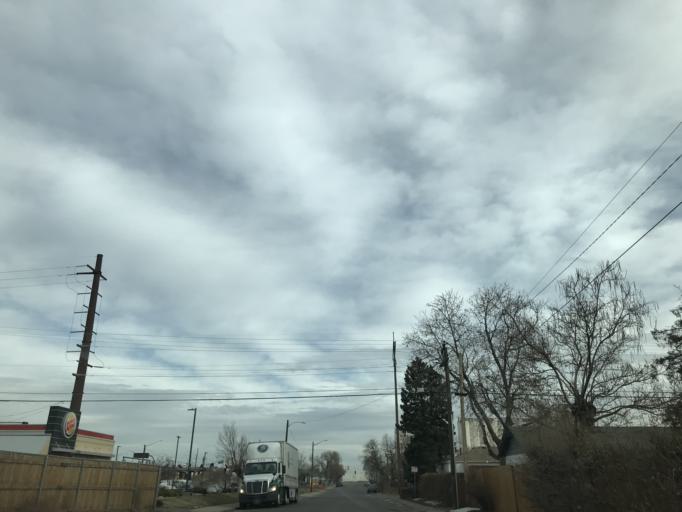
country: US
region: Colorado
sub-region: Adams County
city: Commerce City
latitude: 39.7789
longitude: -104.9518
